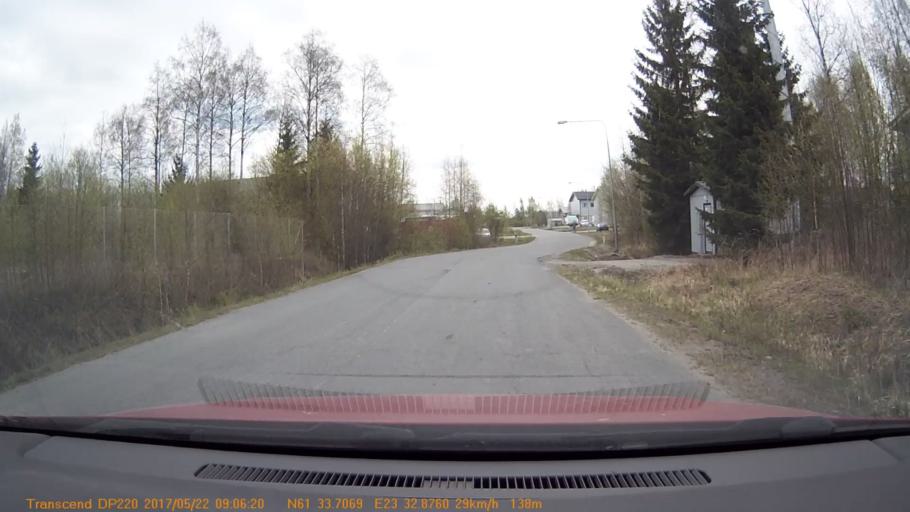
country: FI
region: Pirkanmaa
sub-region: Tampere
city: Yloejaervi
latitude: 61.5618
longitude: 23.5479
